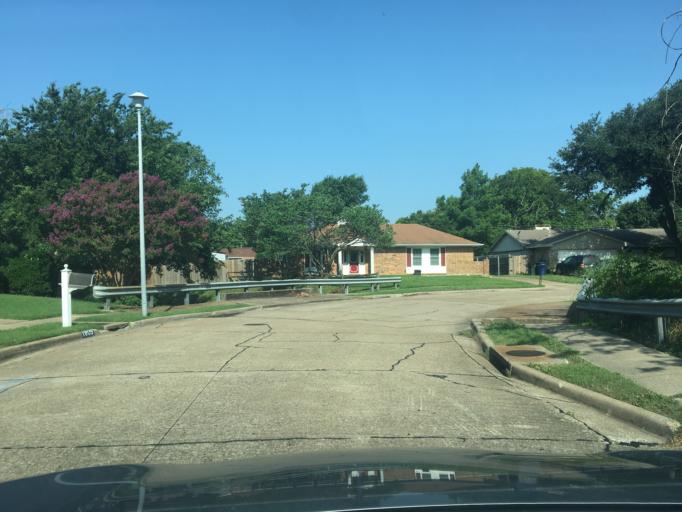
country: US
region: Texas
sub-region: Dallas County
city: Richardson
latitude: 32.9288
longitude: -96.6907
